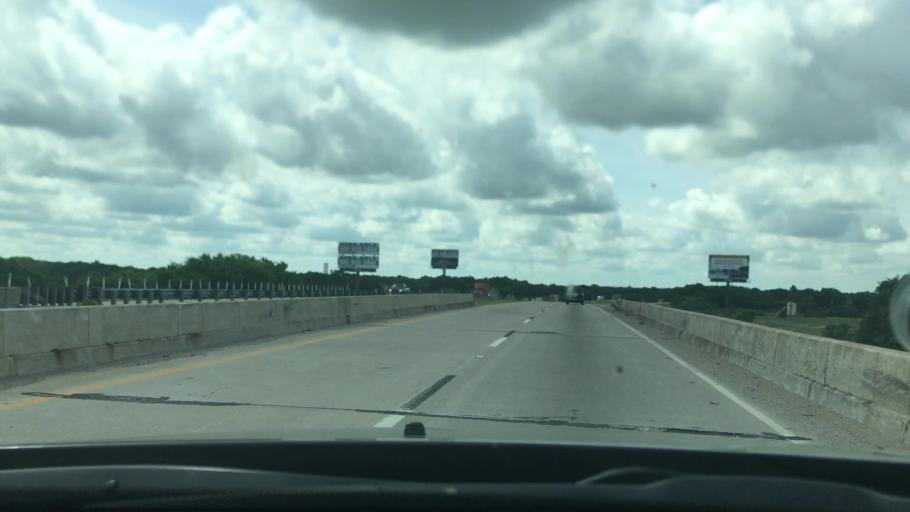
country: US
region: Oklahoma
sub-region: Love County
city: Marietta
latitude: 33.8353
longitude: -97.1319
